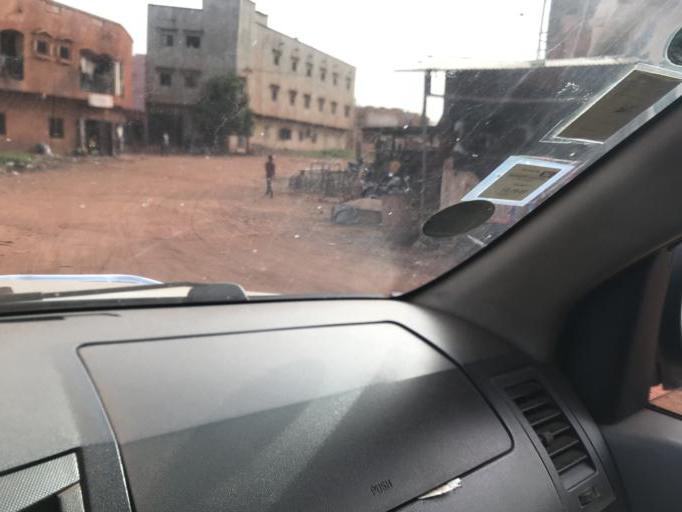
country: ML
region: Bamako
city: Bamako
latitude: 12.5819
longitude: -8.0004
